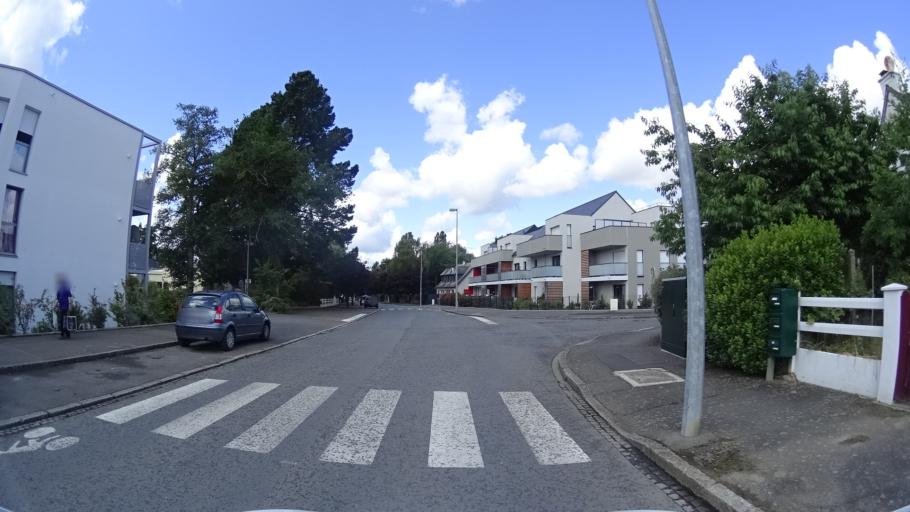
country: FR
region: Brittany
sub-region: Departement d'Ille-et-Vilaine
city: Chartres-de-Bretagne
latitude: 48.0387
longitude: -1.7024
